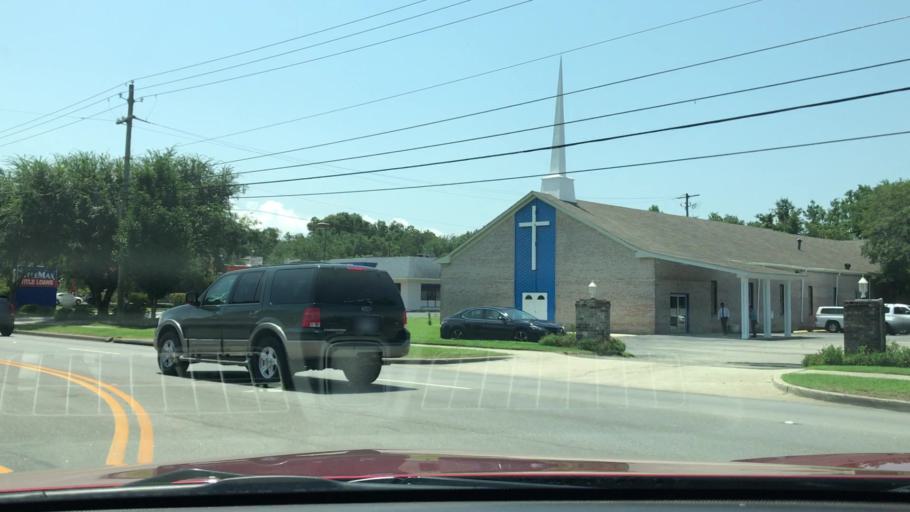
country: US
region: South Carolina
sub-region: Berkeley County
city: Hanahan
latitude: 32.8600
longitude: -80.0461
